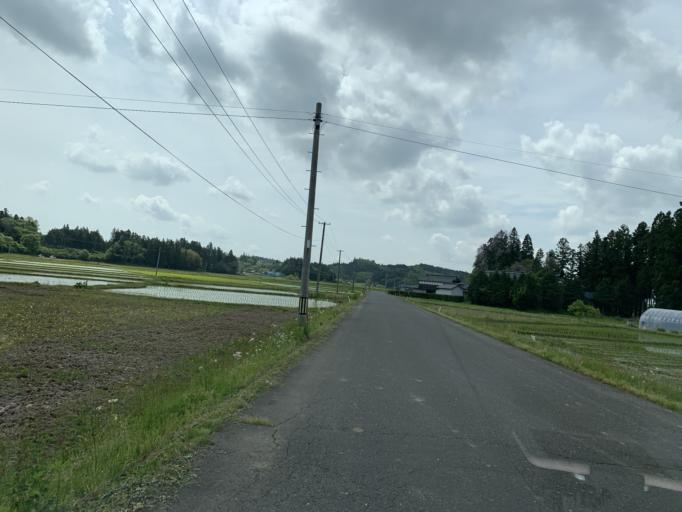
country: JP
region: Iwate
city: Ichinoseki
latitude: 38.8468
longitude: 141.0184
